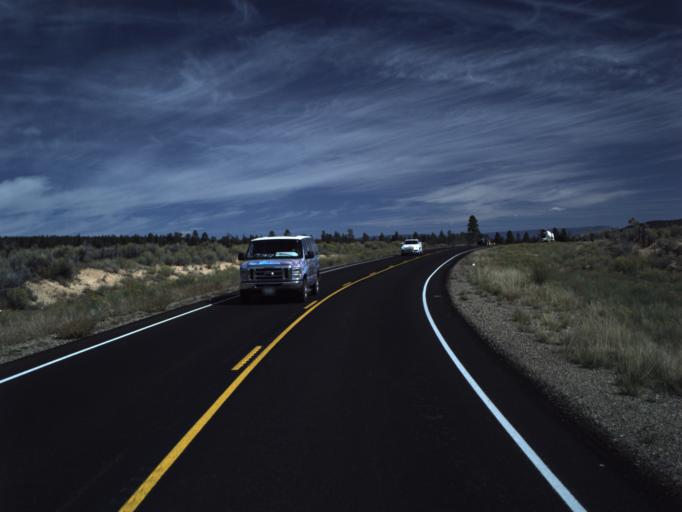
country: US
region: Utah
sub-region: Garfield County
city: Panguitch
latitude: 37.6728
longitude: -111.8283
